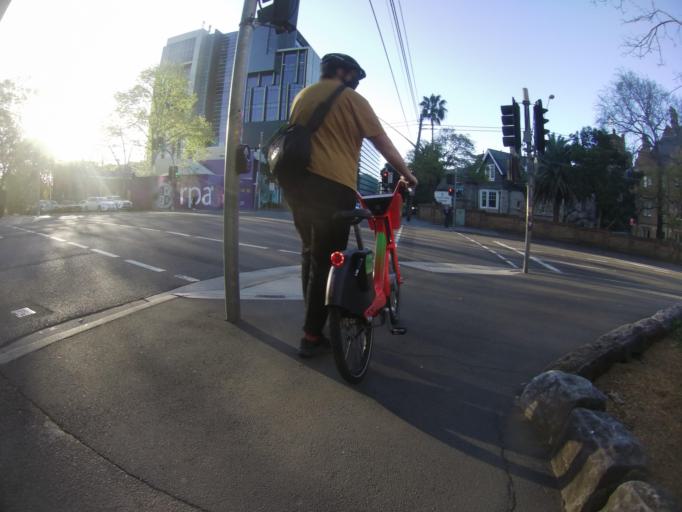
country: AU
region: New South Wales
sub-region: Marrickville
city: Camperdown
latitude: -33.8916
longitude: 151.1830
